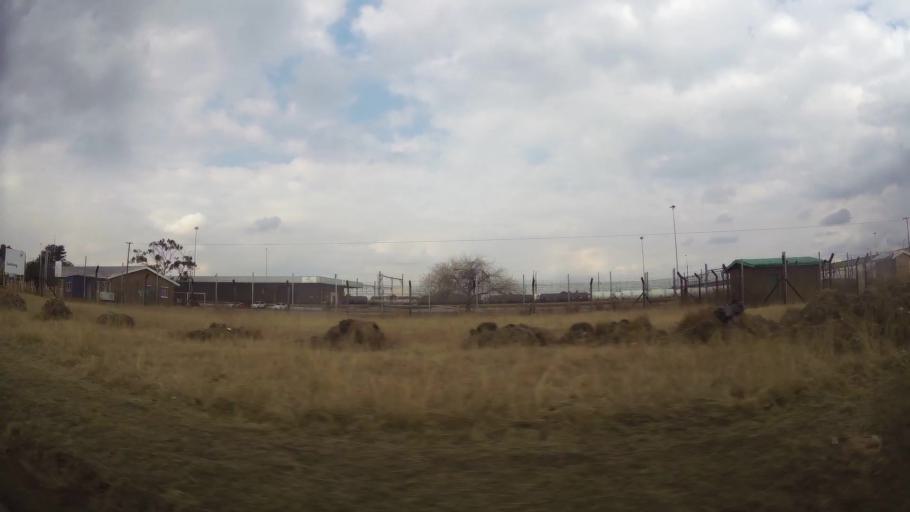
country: ZA
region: Orange Free State
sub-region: Fezile Dabi District Municipality
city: Sasolburg
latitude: -26.8524
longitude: 27.8650
